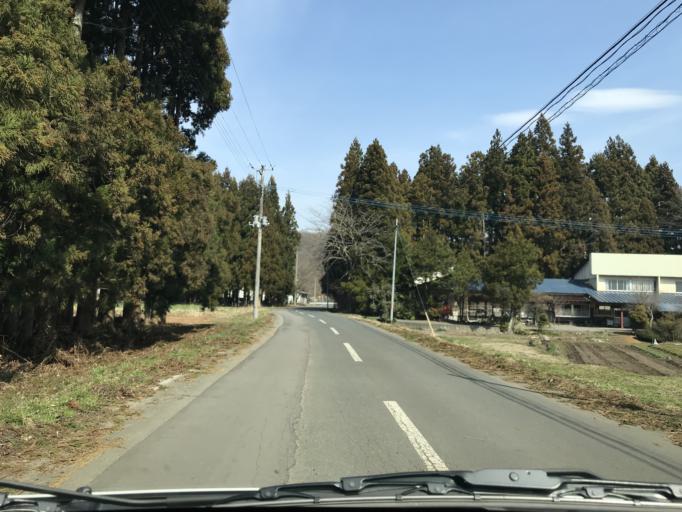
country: JP
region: Iwate
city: Mizusawa
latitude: 39.1252
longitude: 141.0146
